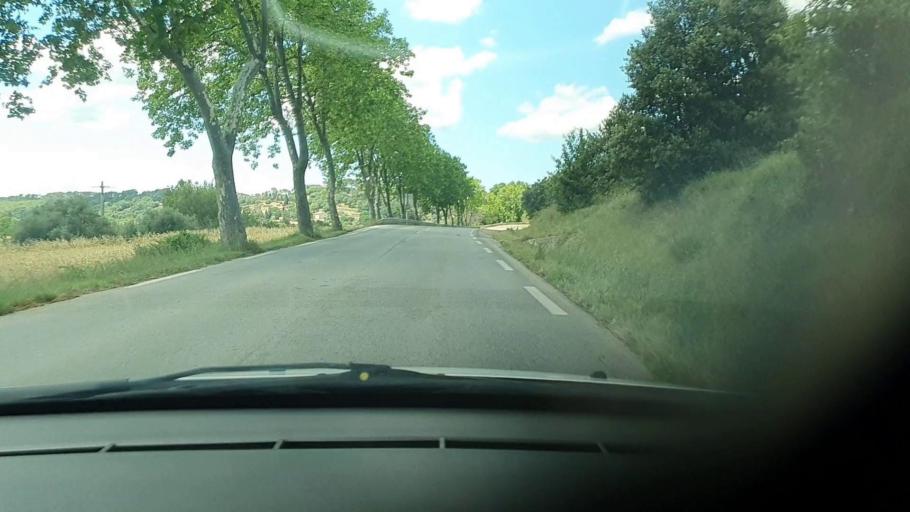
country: FR
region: Languedoc-Roussillon
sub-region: Departement du Gard
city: Montaren-et-Saint-Mediers
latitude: 44.0345
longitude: 4.3638
